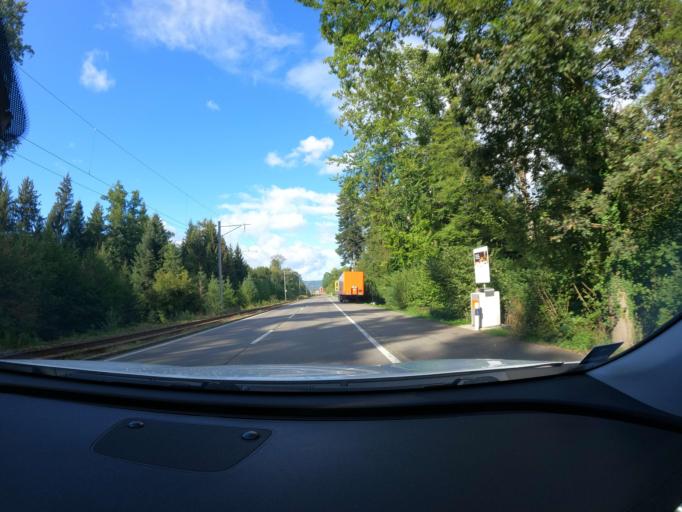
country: CH
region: Aargau
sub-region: Bezirk Lenzburg
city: Staufen
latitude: 47.3665
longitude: 8.1661
